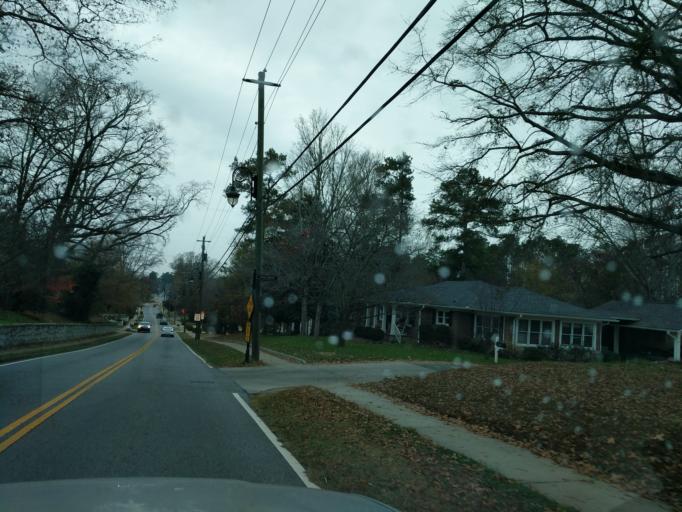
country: US
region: Georgia
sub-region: Gwinnett County
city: Duluth
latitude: 34.0042
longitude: -84.1461
